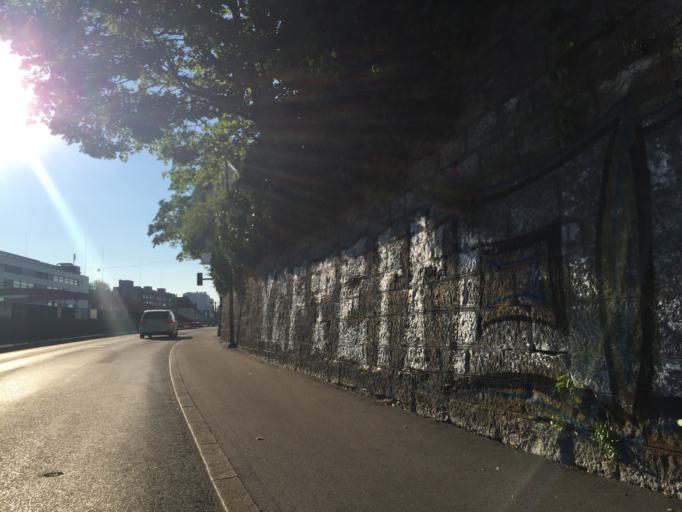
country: CH
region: Bern
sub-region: Bern-Mittelland District
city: Bern
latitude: 46.9485
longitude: 7.4292
